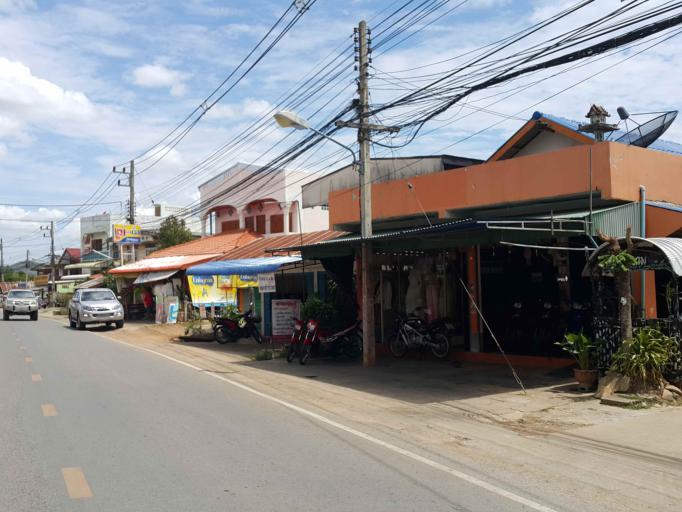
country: TH
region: Sukhothai
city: Thung Saliam
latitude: 17.3180
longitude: 99.5492
